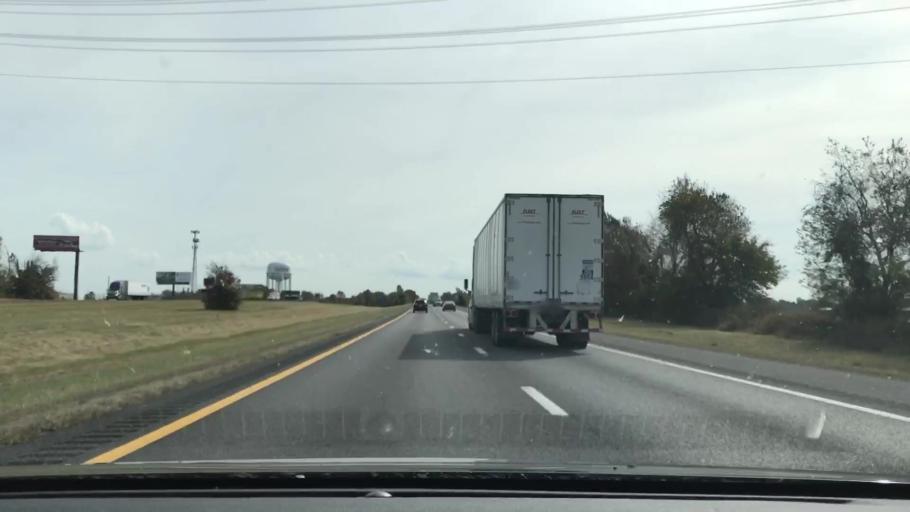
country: US
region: Tennessee
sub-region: Montgomery County
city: Clarksville
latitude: 36.5929
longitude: -87.2775
